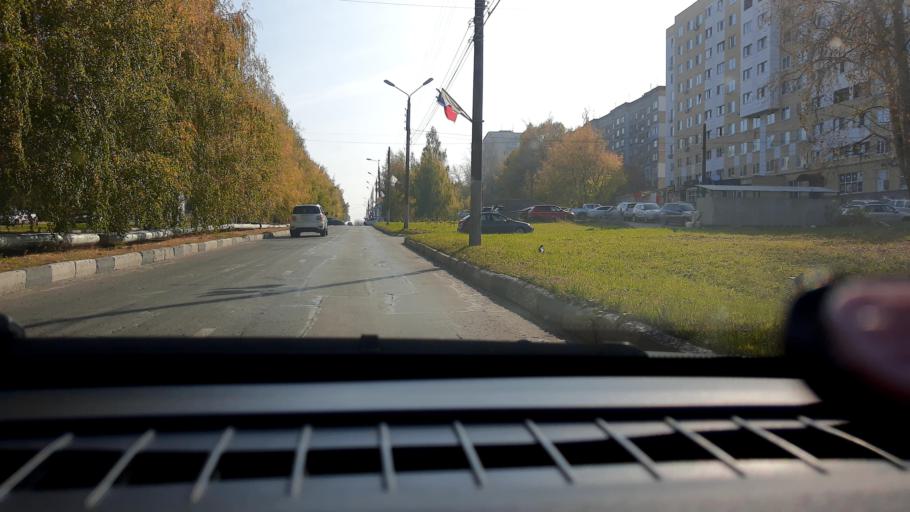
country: RU
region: Nizjnij Novgorod
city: Kstovo
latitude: 56.1582
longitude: 44.2094
